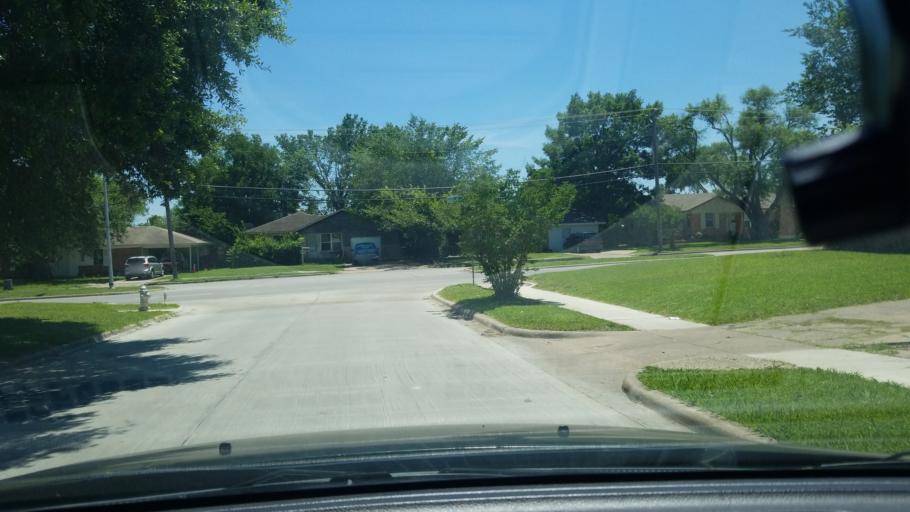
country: US
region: Texas
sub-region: Dallas County
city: Mesquite
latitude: 32.7712
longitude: -96.6052
